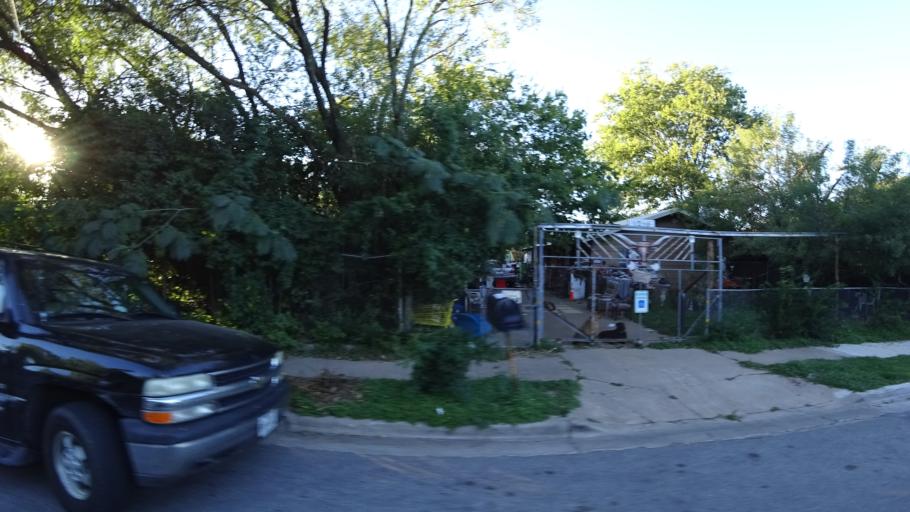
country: US
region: Texas
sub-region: Travis County
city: Austin
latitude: 30.2325
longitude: -97.7023
